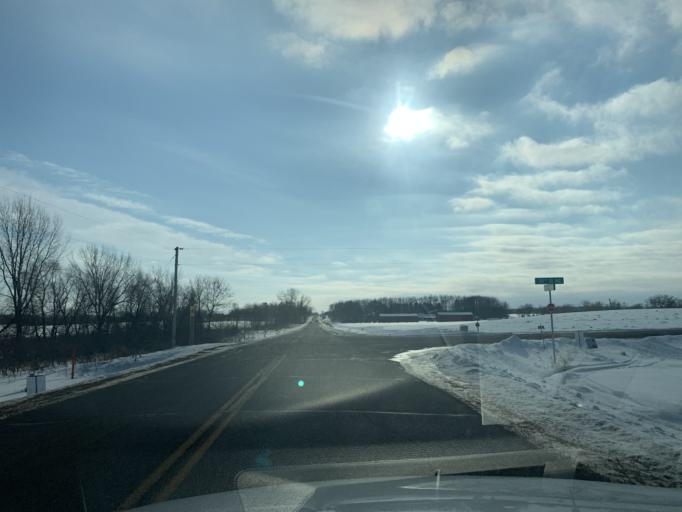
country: US
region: Minnesota
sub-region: Wright County
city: Buffalo
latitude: 45.1944
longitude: -93.8272
